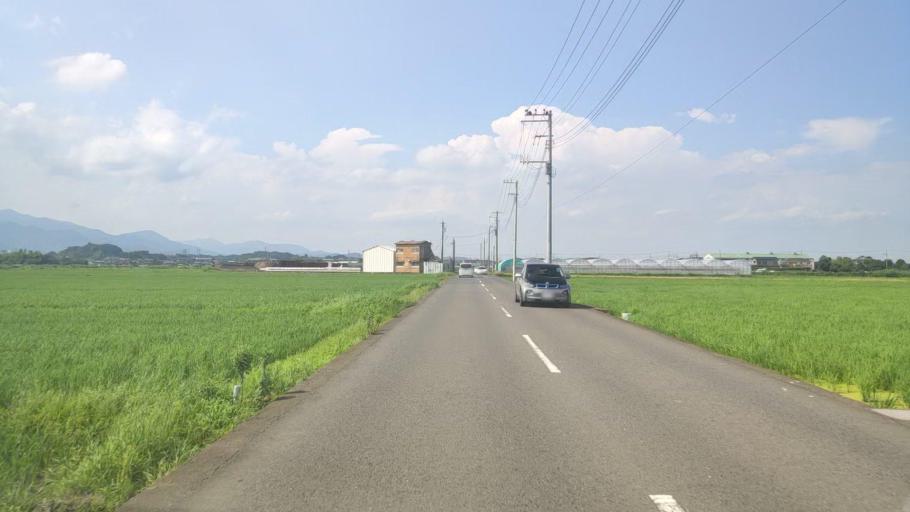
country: JP
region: Kanagawa
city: Isehara
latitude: 35.3592
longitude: 139.3160
